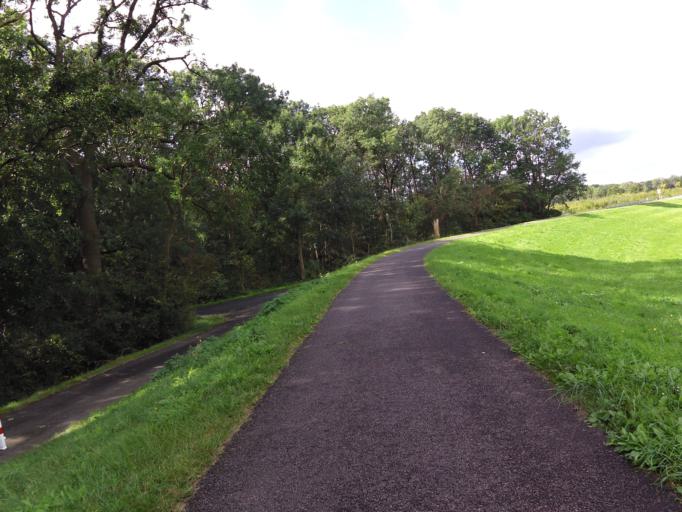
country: DE
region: Saxony-Anhalt
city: Plotzky
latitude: 52.0386
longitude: 11.8273
